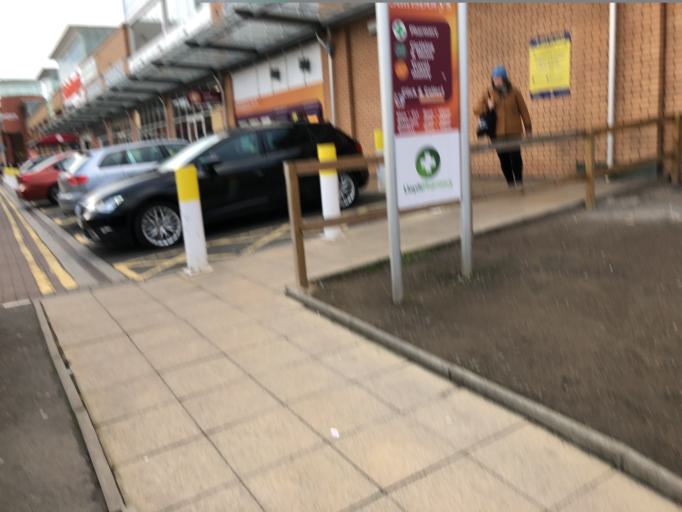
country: GB
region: Scotland
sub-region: West Lothian
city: Seafield
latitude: 55.9585
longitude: -3.1638
